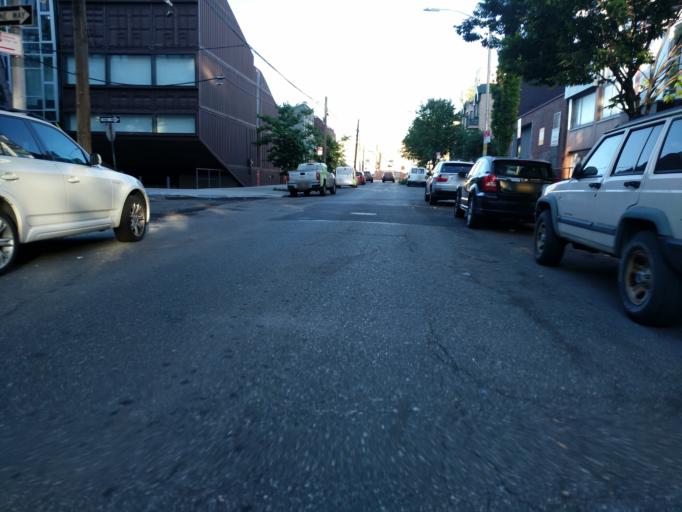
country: US
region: New York
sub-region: Queens County
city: Long Island City
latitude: 40.7191
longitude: -73.9419
